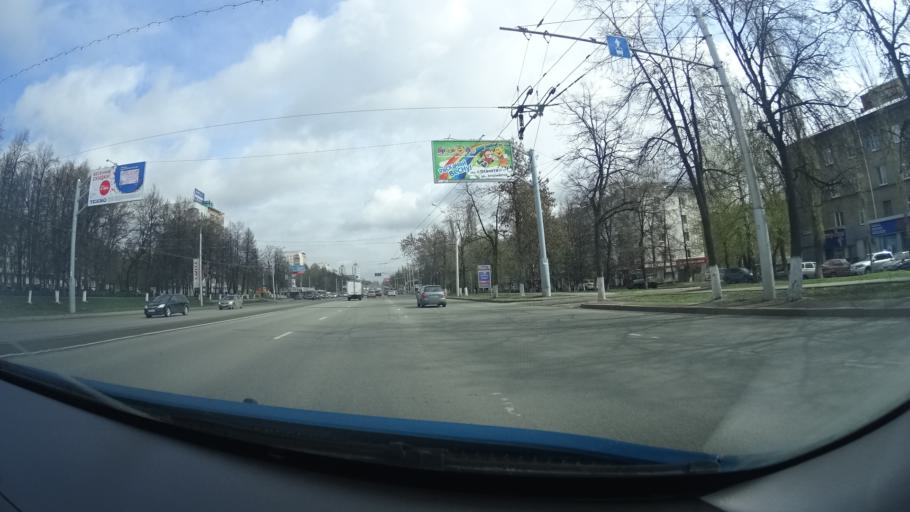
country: RU
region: Bashkortostan
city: Ufa
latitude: 54.7538
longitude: 55.9992
